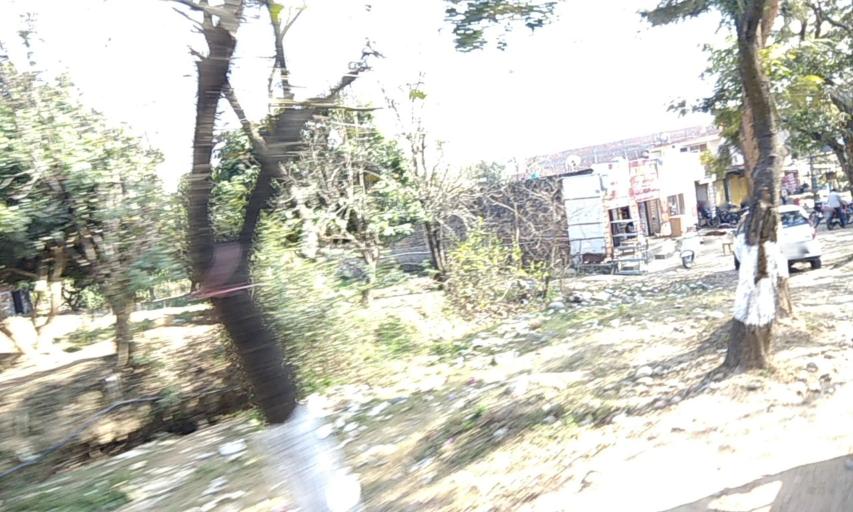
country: IN
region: Himachal Pradesh
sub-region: Kangra
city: Yol
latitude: 32.2161
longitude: 76.1800
